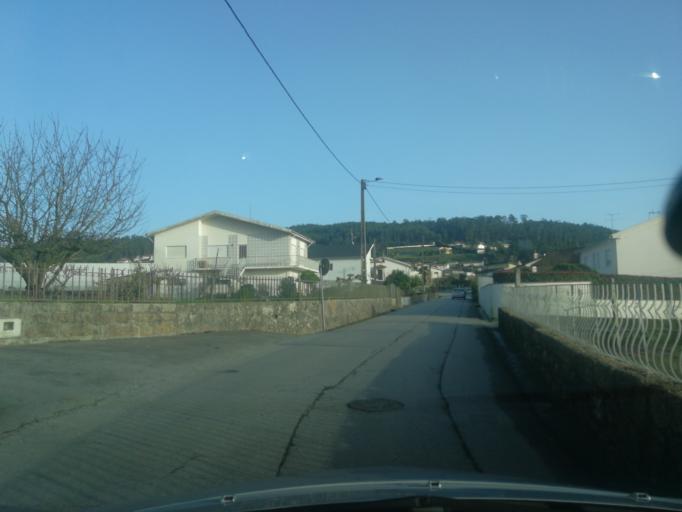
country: PT
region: Braga
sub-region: Barcelos
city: Galegos
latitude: 41.5174
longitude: -8.5667
